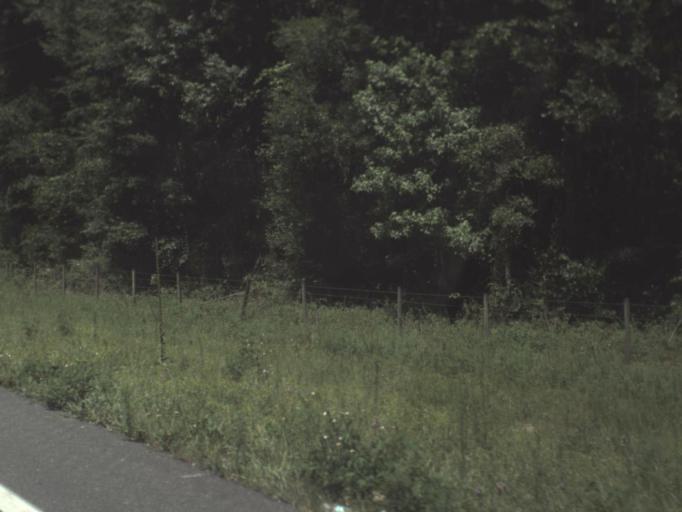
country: US
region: Florida
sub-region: Alachua County
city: High Springs
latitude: 29.9008
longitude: -82.8600
